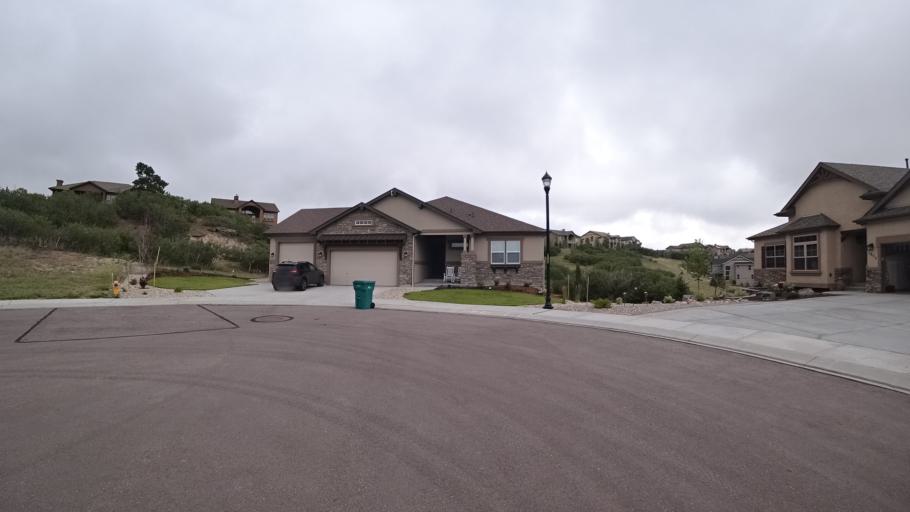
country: US
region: Colorado
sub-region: El Paso County
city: Gleneagle
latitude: 39.0147
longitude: -104.7912
